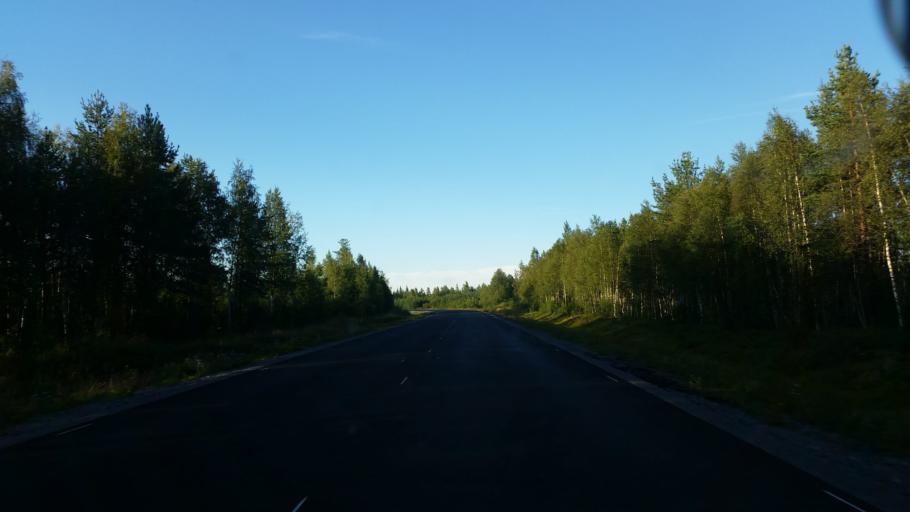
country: SE
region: Vaesterbotten
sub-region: Dorotea Kommun
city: Dorotea
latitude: 64.3332
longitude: 16.6371
